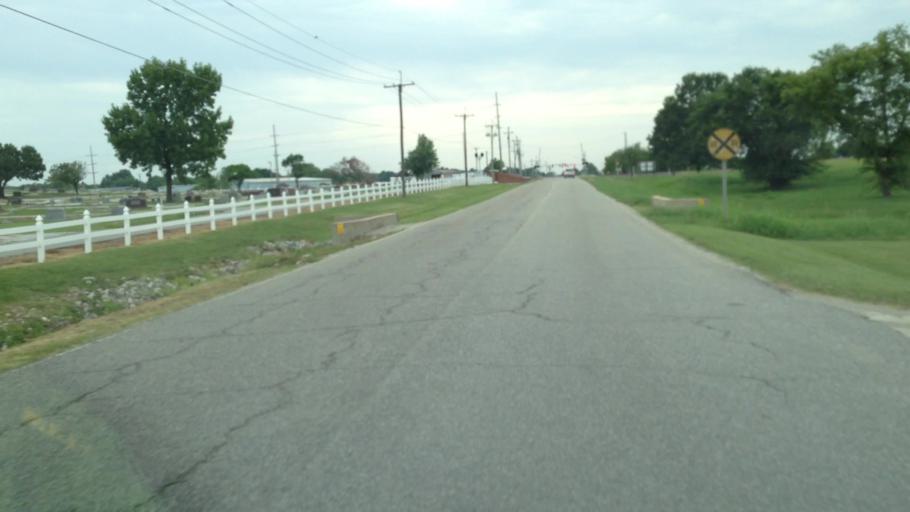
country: US
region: Oklahoma
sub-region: Craig County
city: Vinita
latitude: 36.6560
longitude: -95.1398
